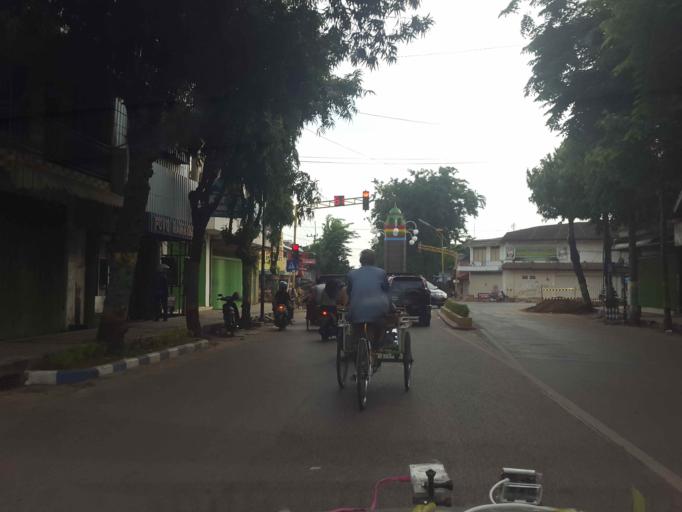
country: ID
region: East Java
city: Sumenep
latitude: -7.0061
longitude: 113.8600
